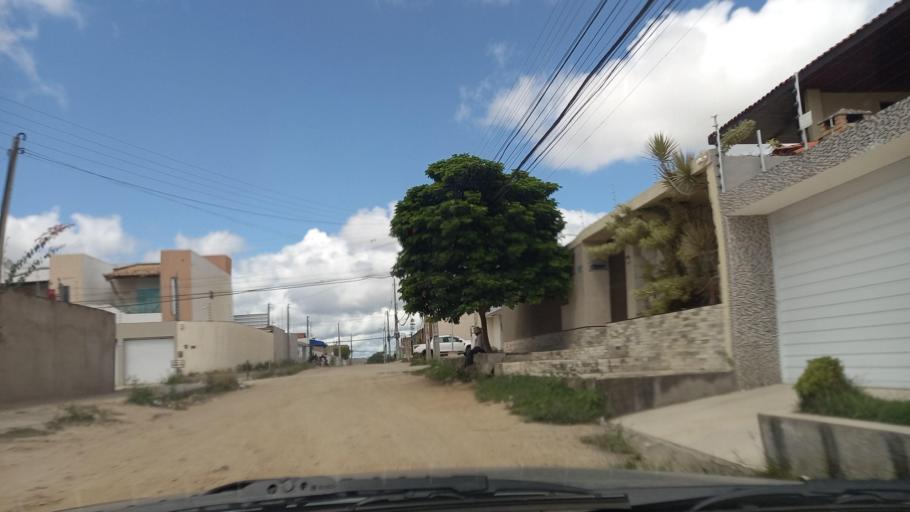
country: BR
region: Pernambuco
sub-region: Caruaru
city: Caruaru
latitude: -8.2574
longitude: -35.9794
